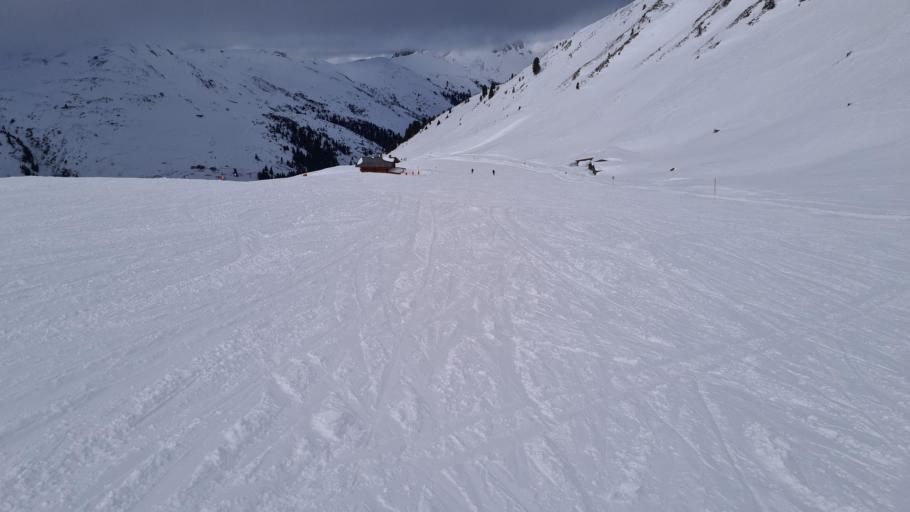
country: AT
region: Salzburg
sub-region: Politischer Bezirk Zell am See
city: Neukirchen am Grossvenediger
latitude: 47.2896
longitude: 12.2931
